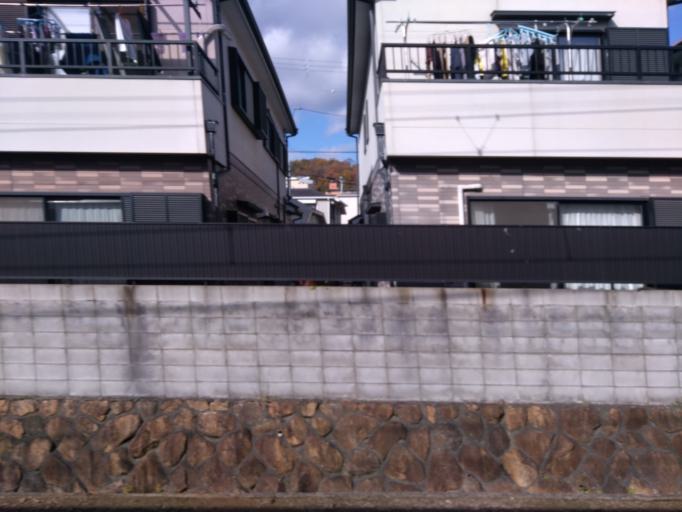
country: JP
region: Hyogo
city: Takarazuka
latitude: 34.8178
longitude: 135.3652
